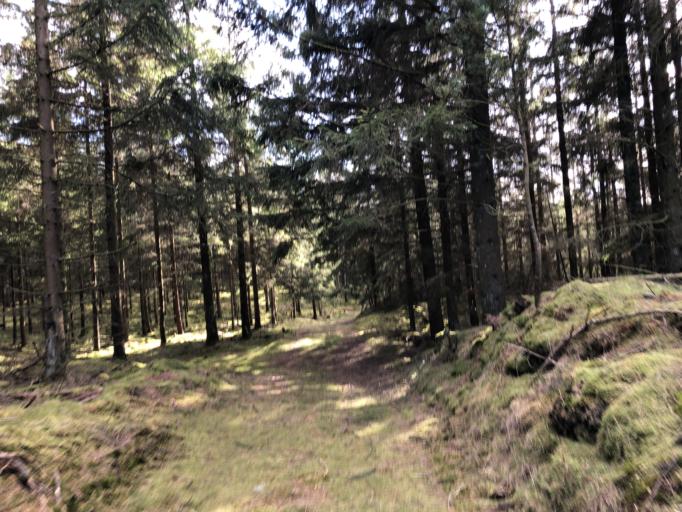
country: DK
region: Central Jutland
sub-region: Holstebro Kommune
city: Ulfborg
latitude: 56.2166
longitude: 8.3967
